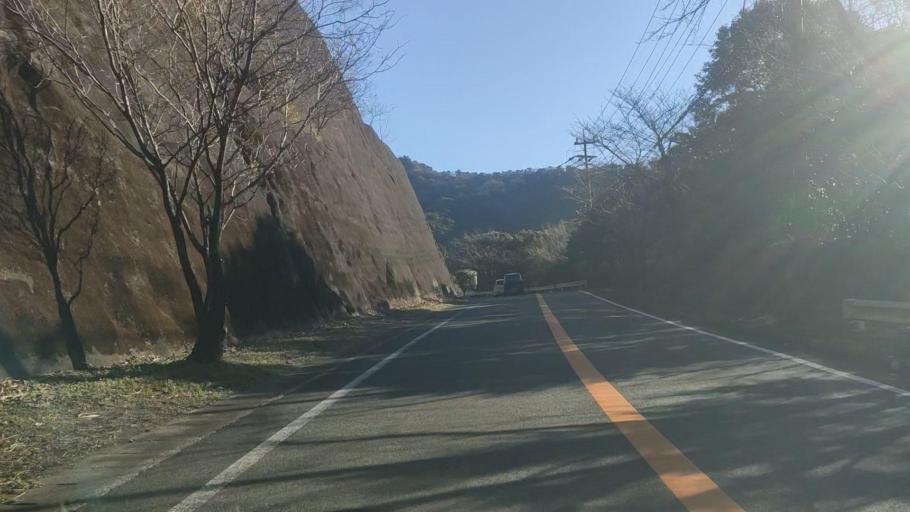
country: JP
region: Miyazaki
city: Nobeoka
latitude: 32.6262
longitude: 131.7135
